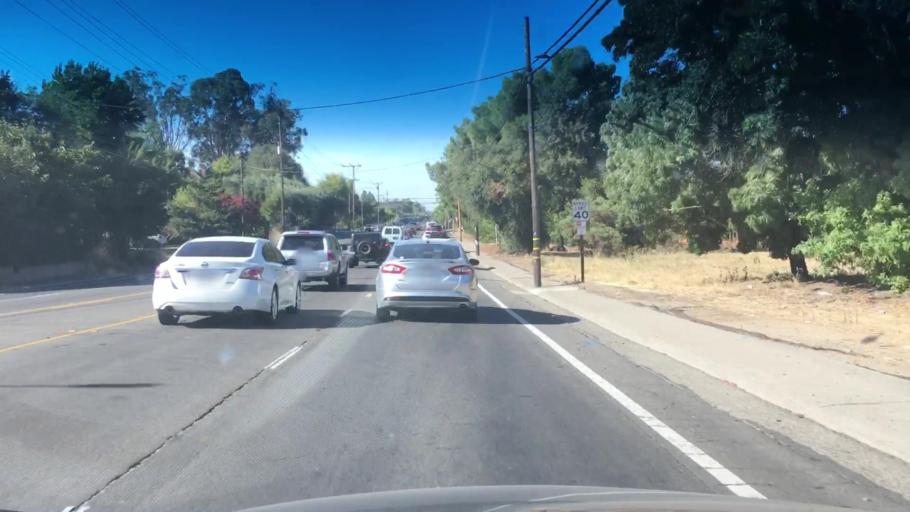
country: US
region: California
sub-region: Sacramento County
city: Orangevale
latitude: 38.6588
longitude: -121.2256
